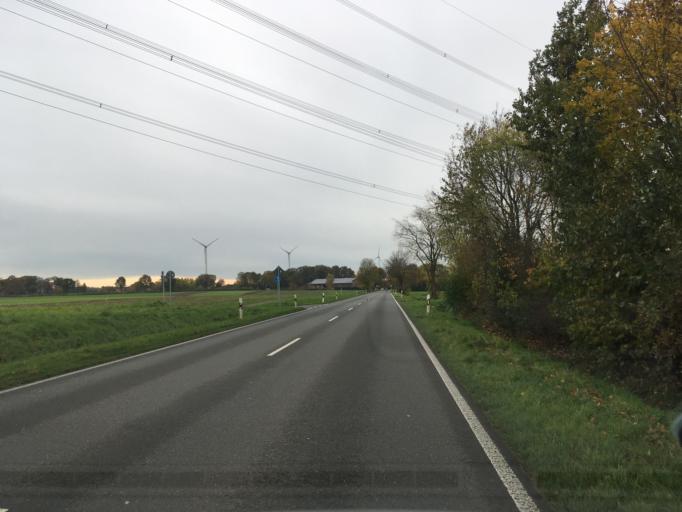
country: DE
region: North Rhine-Westphalia
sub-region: Regierungsbezirk Munster
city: Heiden
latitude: 51.8070
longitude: 6.9502
